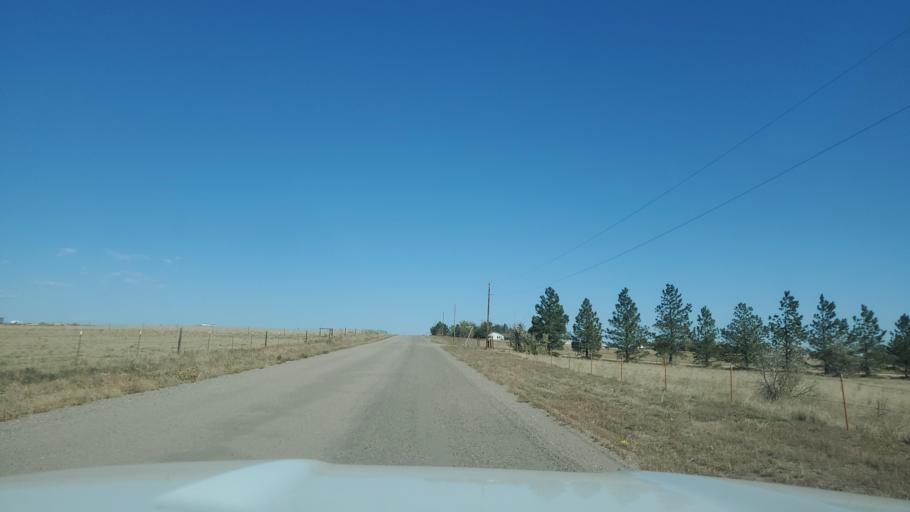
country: US
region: Colorado
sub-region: Adams County
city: Bennett
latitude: 39.7681
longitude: -104.3769
